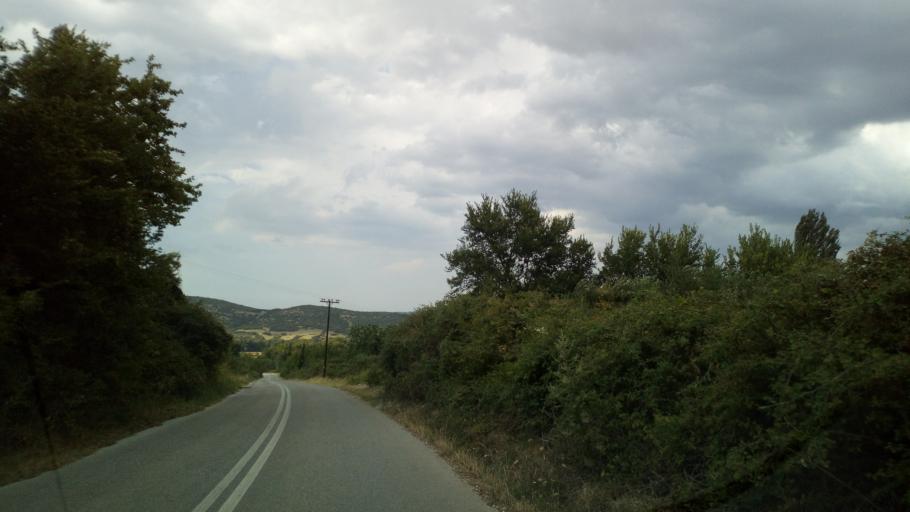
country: GR
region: Central Macedonia
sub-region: Nomos Chalkidikis
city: Galatista
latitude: 40.5160
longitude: 23.3470
